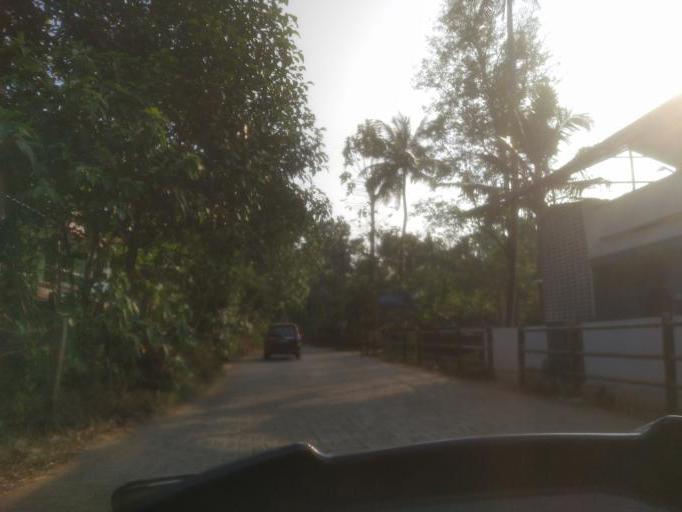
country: IN
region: Kerala
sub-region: Ernakulam
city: Piravam
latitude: 9.8163
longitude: 76.4999
